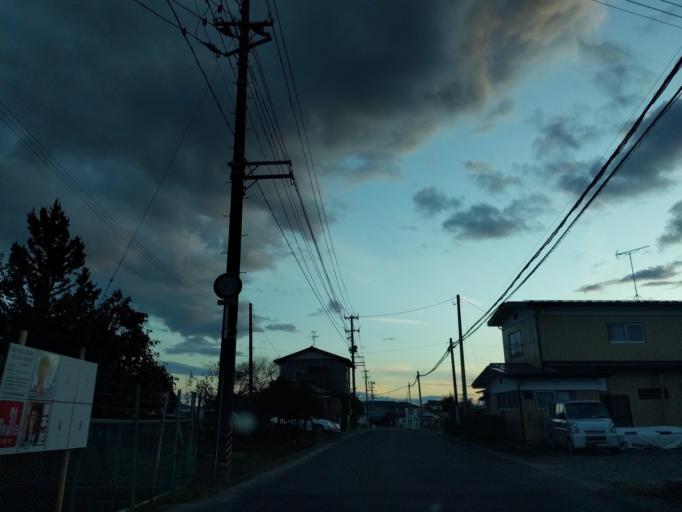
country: JP
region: Fukushima
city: Motomiya
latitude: 37.5117
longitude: 140.4054
